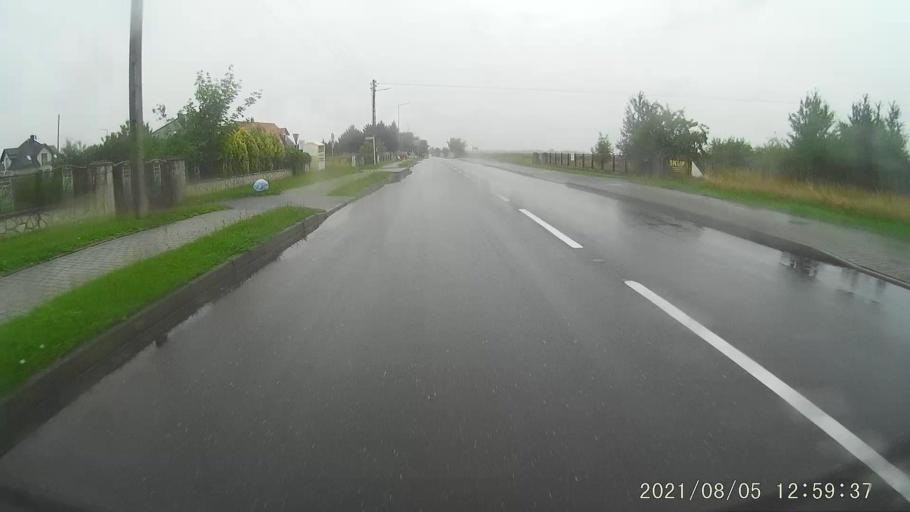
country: PL
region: Opole Voivodeship
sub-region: Powiat krapkowicki
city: Krapkowice
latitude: 50.4782
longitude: 17.9894
